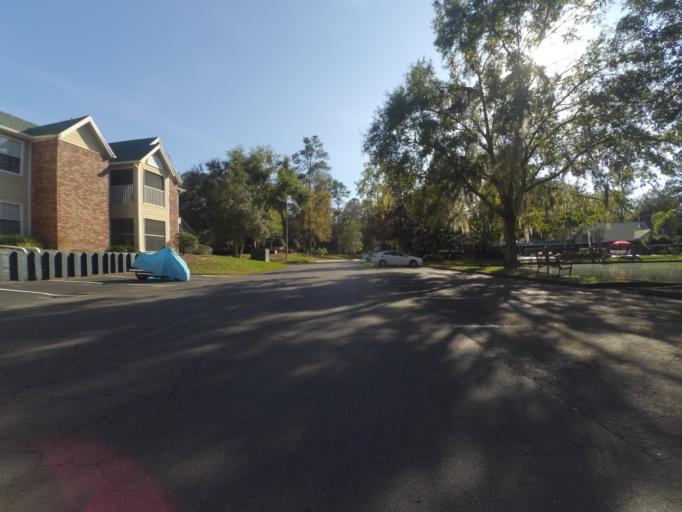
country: US
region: Florida
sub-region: Alachua County
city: Gainesville
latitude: 29.6148
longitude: -82.3573
